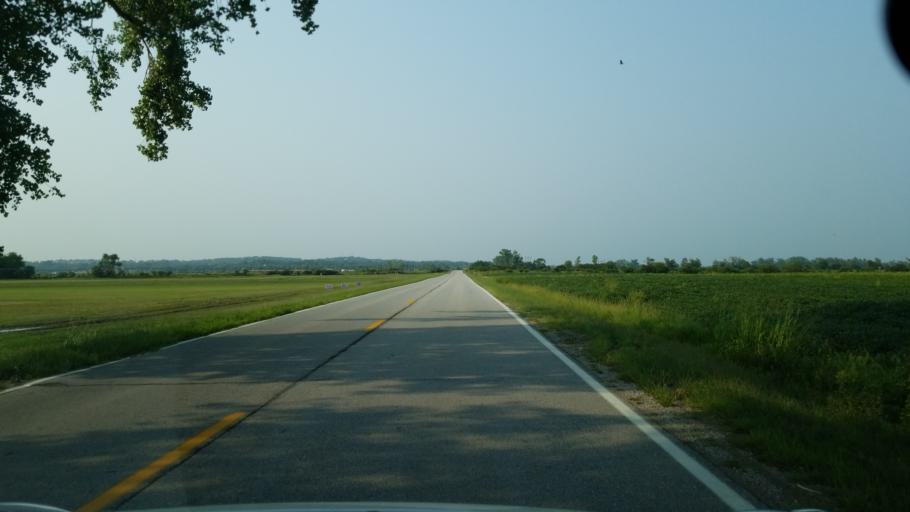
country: US
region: Nebraska
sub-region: Sarpy County
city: Bellevue
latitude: 41.1045
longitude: -95.8899
